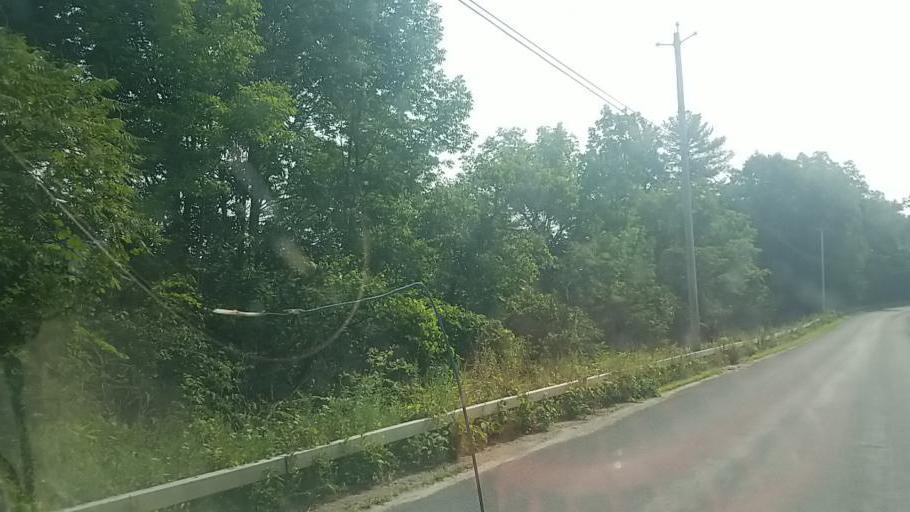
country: US
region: New York
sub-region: Montgomery County
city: Fonda
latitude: 42.9687
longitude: -74.4253
